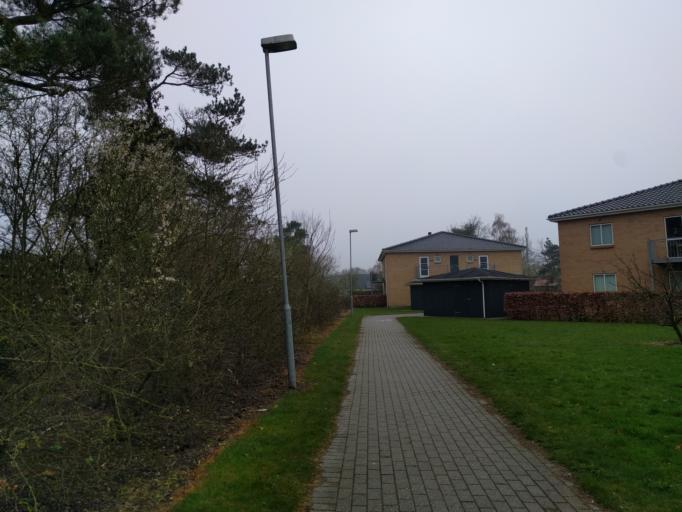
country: DK
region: Central Jutland
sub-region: Arhus Kommune
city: Lystrup
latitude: 56.2073
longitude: 10.2390
